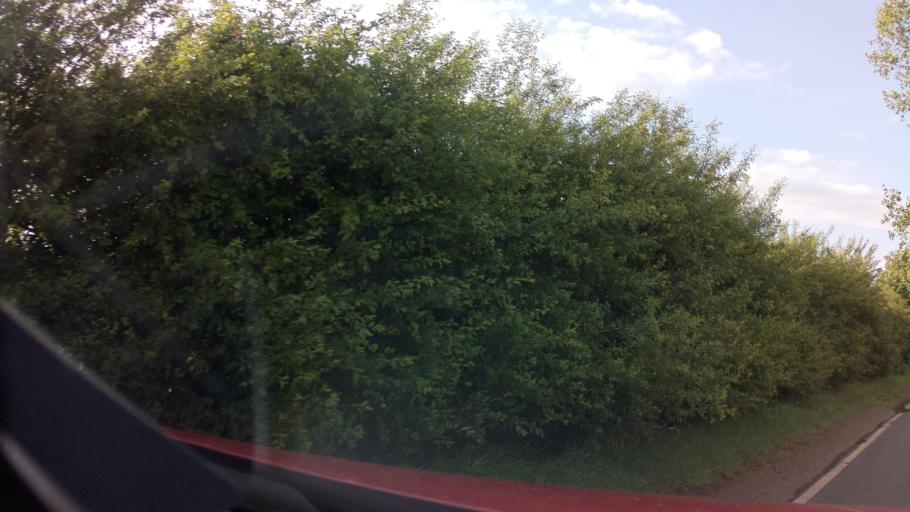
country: GB
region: England
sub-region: Lincolnshire
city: Great Gonerby
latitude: 52.9770
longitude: -0.6797
